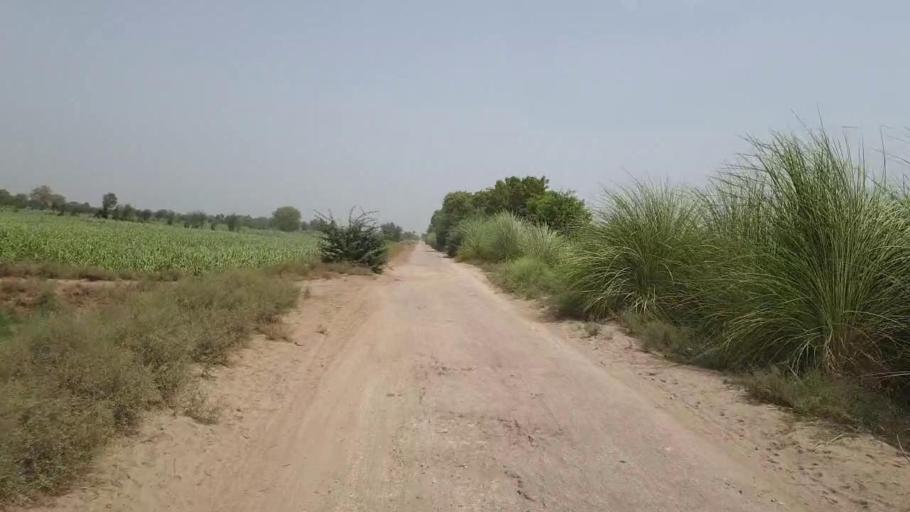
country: PK
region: Sindh
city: Nawabshah
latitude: 26.2963
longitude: 68.3065
